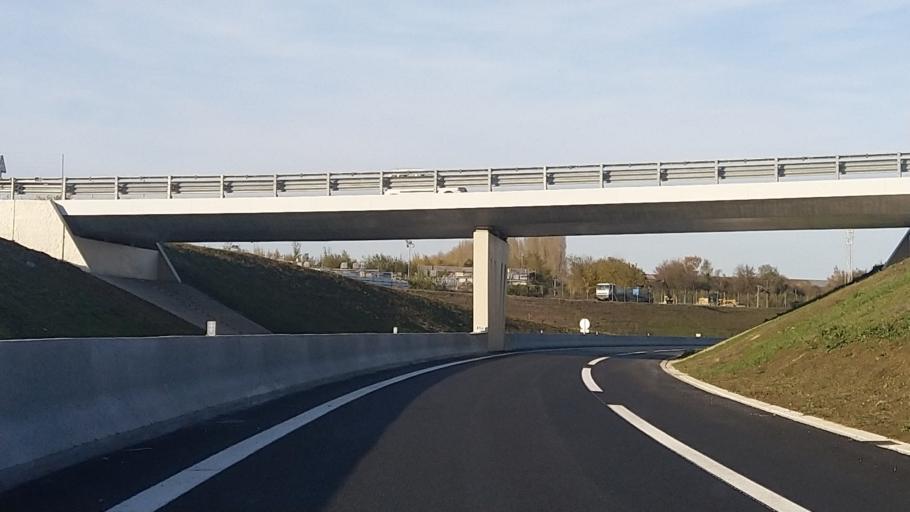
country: FR
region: Ile-de-France
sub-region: Departement du Val-d'Oise
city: Montsoult
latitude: 49.0661
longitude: 2.3313
